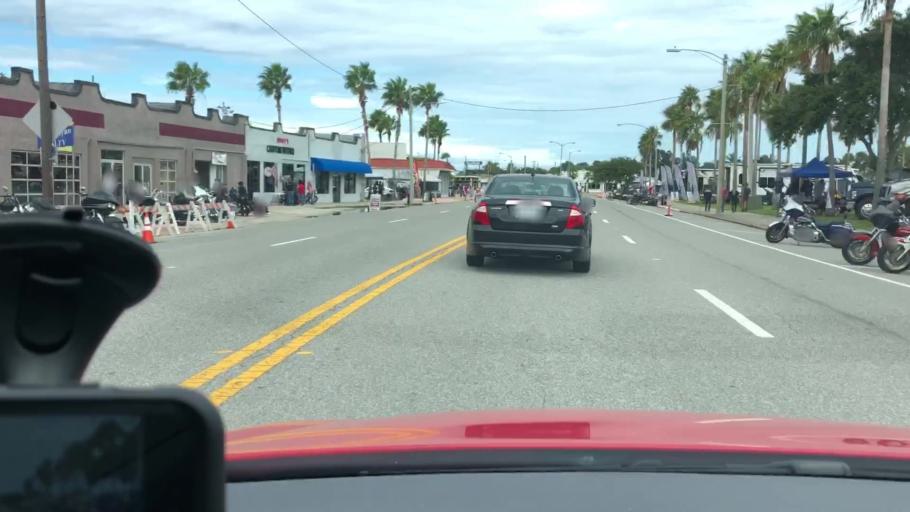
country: US
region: Florida
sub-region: Volusia County
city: Daytona Beach
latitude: 29.2194
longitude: -81.0225
